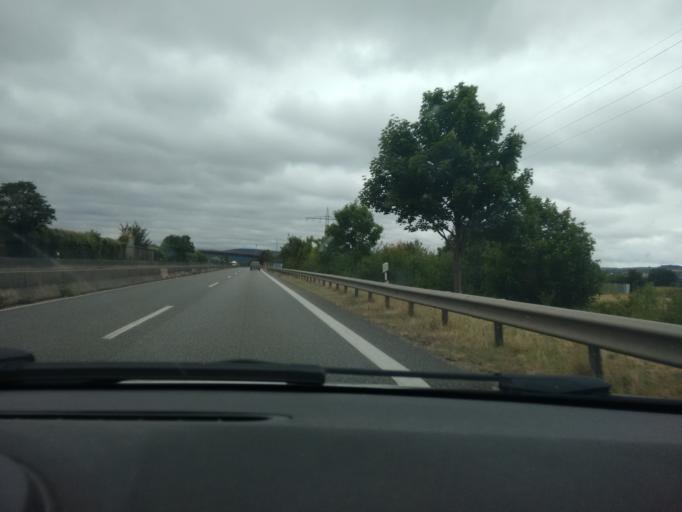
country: DE
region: Rheinland-Pfalz
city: Bretzenheim
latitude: 49.8672
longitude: 7.9088
